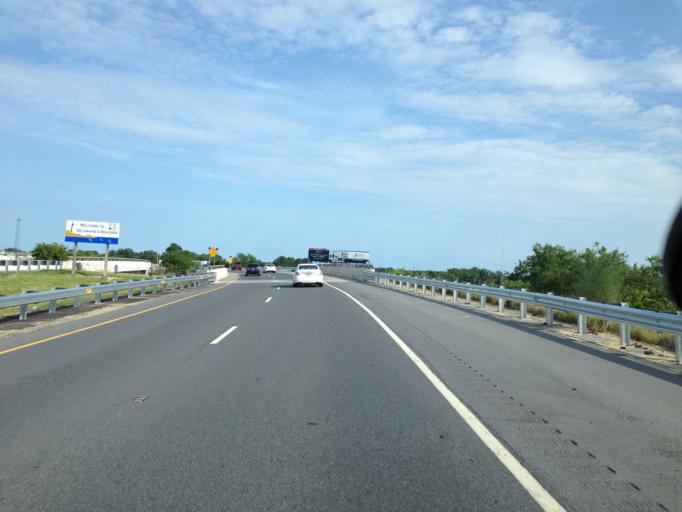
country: US
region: Delaware
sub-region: Sussex County
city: Lewes
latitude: 38.7517
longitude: -75.1902
